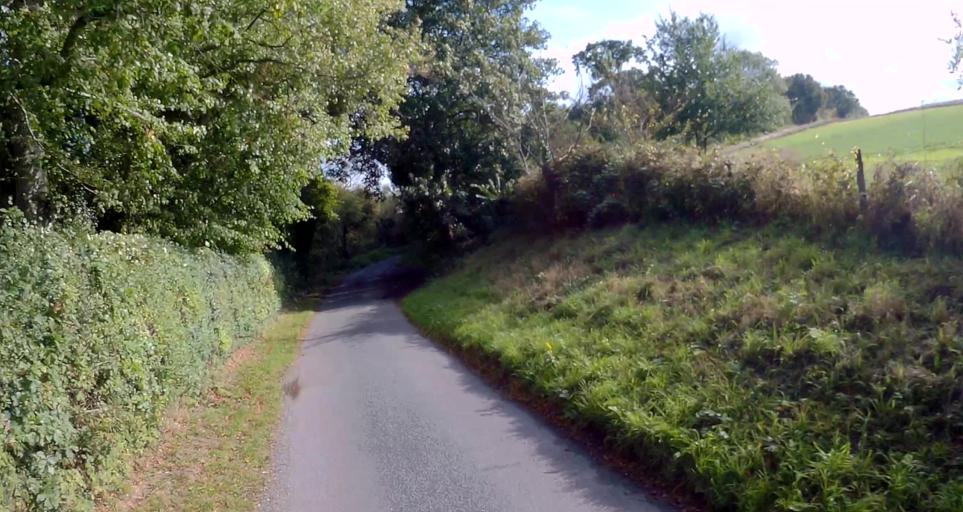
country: GB
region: England
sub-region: Hampshire
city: Kings Worthy
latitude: 51.0906
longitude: -1.2229
